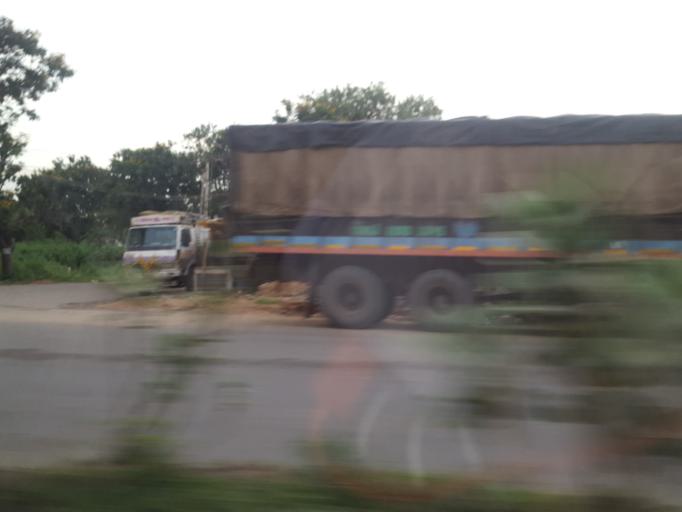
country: IN
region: Telangana
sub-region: Medak
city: Serilingampalle
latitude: 17.5171
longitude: 78.3571
